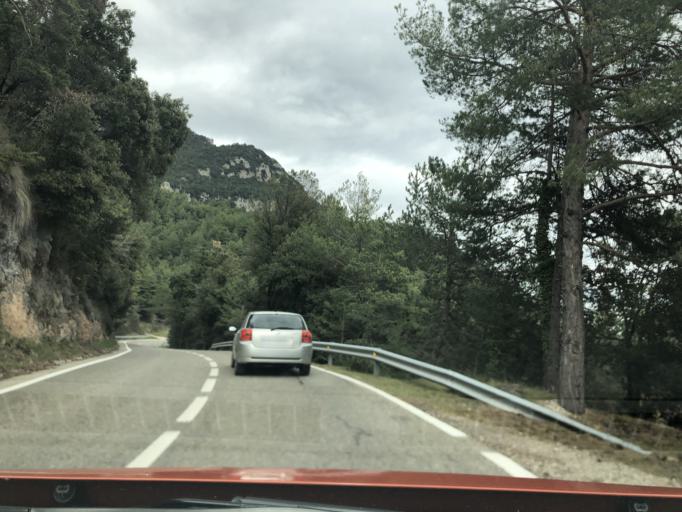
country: ES
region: Catalonia
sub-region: Provincia de Barcelona
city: Castellar del Riu
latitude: 42.0953
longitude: 1.7929
